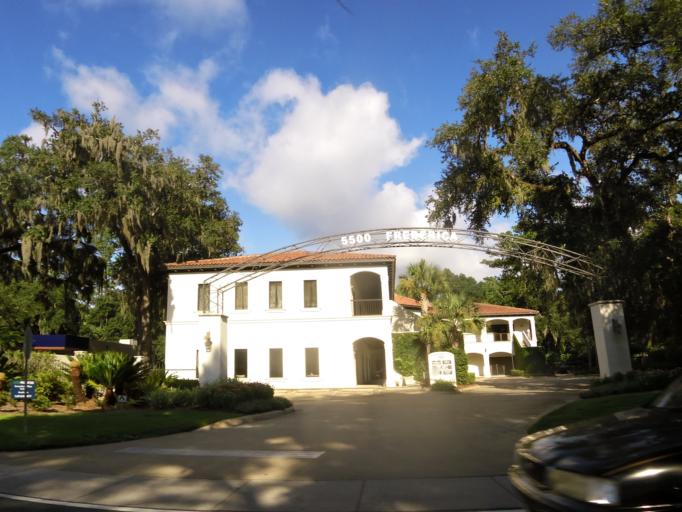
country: US
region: Georgia
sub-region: Glynn County
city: Saint Simon Mills
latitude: 31.2052
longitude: -81.3759
